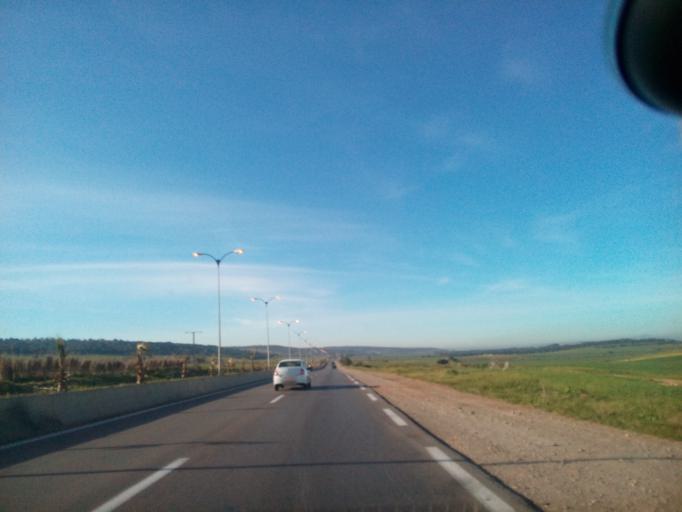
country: DZ
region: Mostaganem
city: Mostaganem
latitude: 35.8208
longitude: -0.0182
